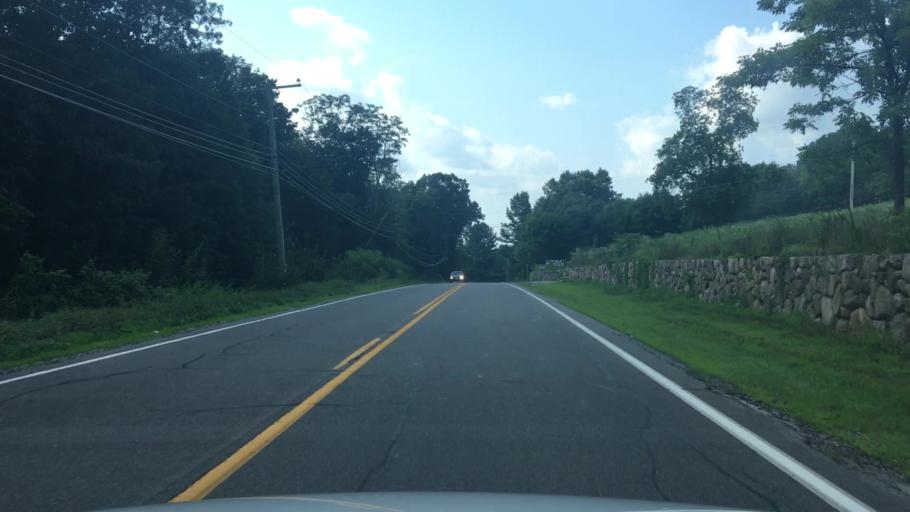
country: US
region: New Hampshire
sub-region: Rockingham County
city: Auburn
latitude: 42.9731
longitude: -71.3668
